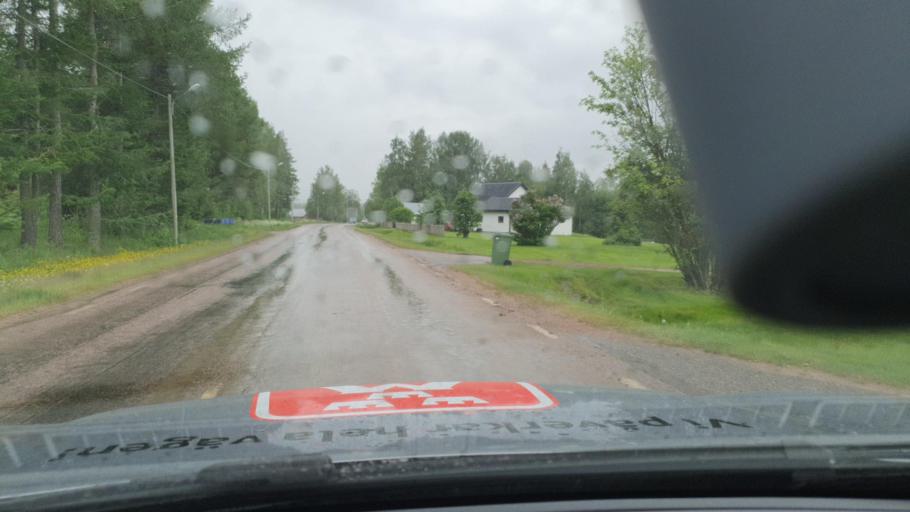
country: SE
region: Norrbotten
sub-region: Overkalix Kommun
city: OEverkalix
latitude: 66.3903
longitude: 22.9370
